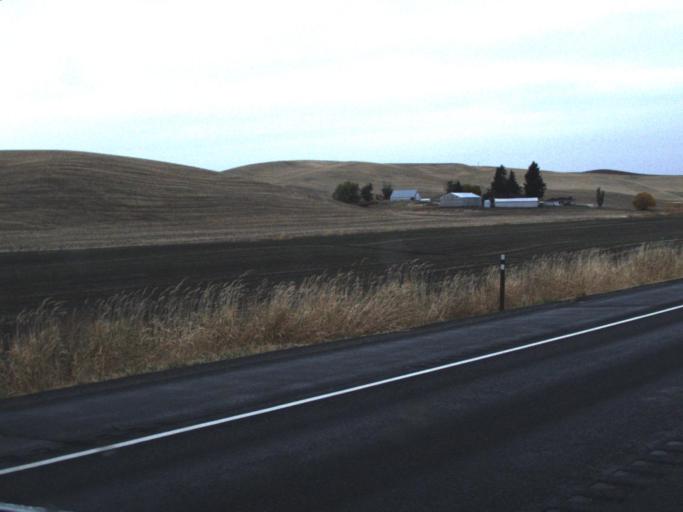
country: US
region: Washington
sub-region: Whitman County
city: Colfax
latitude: 46.8094
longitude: -117.3191
